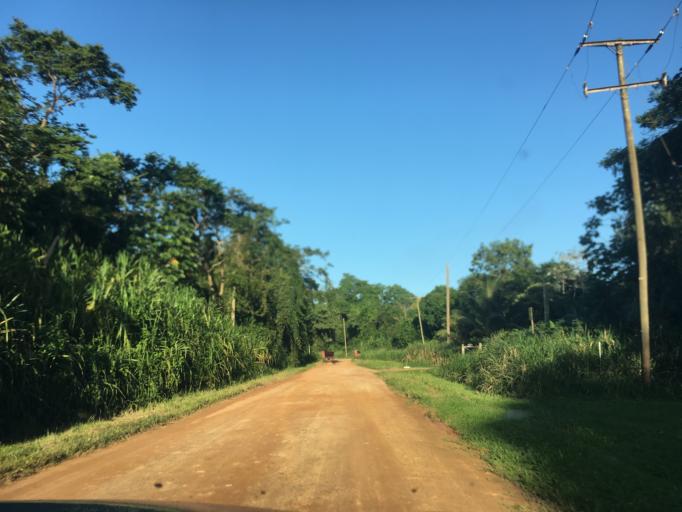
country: BZ
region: Stann Creek
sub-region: Dangriga
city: Dangriga
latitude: 16.8321
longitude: -88.2870
